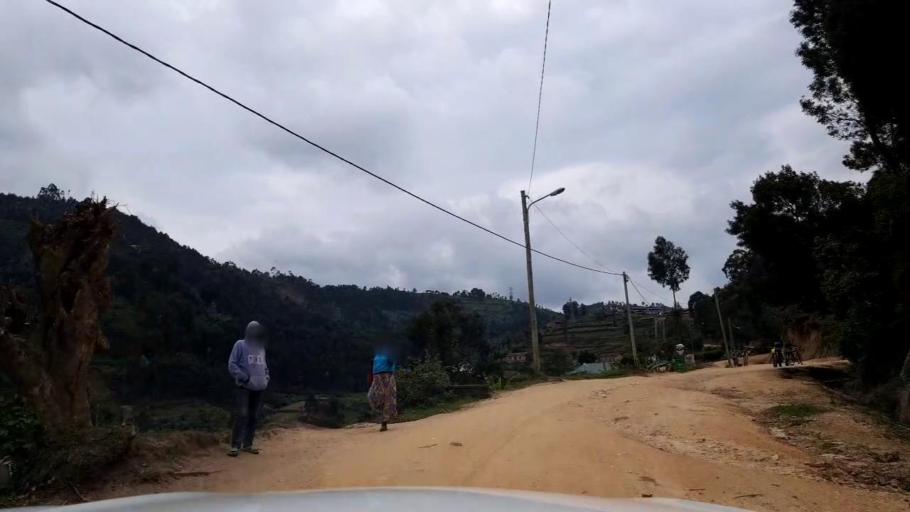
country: RW
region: Western Province
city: Kibuye
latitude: -1.9654
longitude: 29.3894
